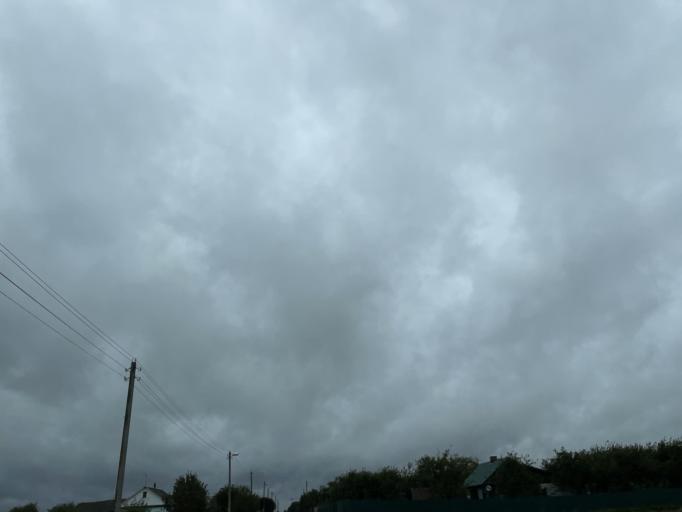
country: BY
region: Brest
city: Lyakhavichy
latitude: 53.1860
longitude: 26.2534
